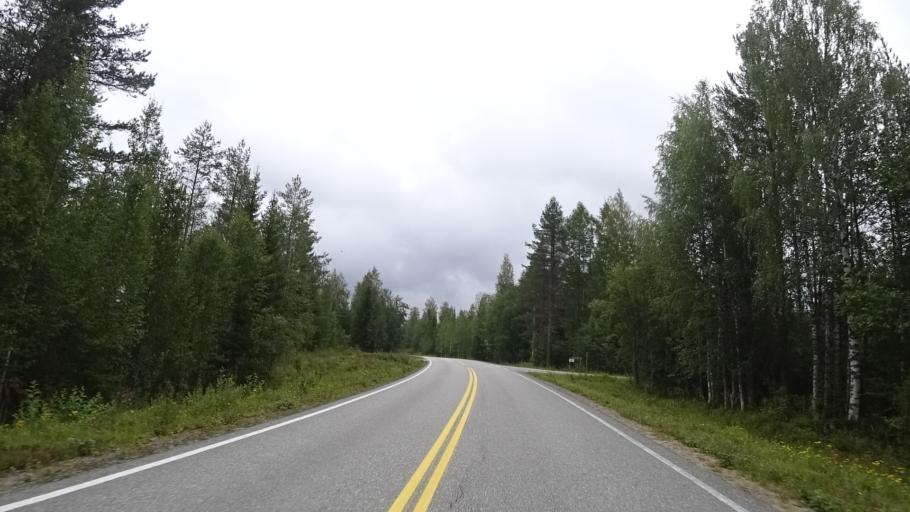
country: FI
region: North Karelia
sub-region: Joensuu
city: Ilomantsi
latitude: 63.2595
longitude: 30.6687
